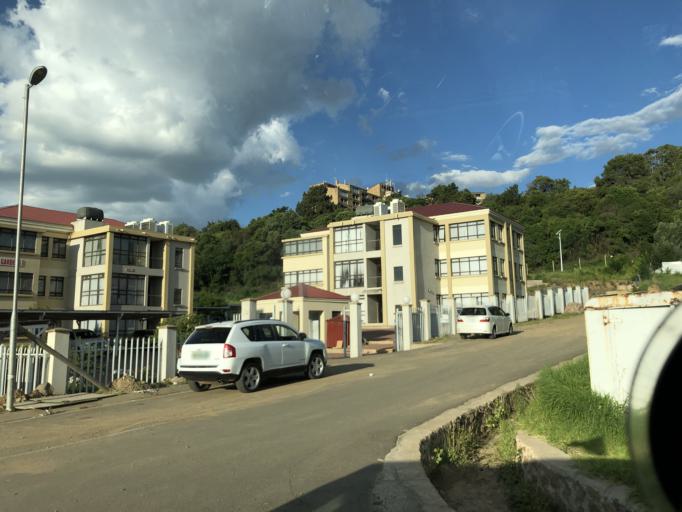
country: LS
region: Maseru
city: Maseru
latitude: -29.3194
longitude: 27.4864
